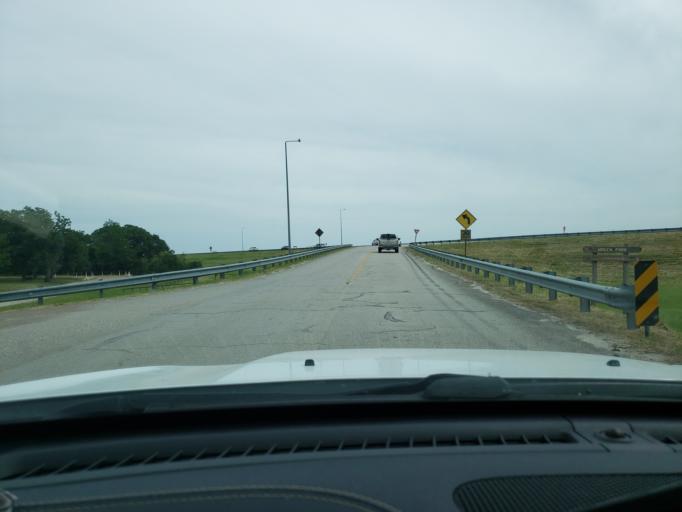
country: US
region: Texas
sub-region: Burleson County
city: Somerville
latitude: 30.3361
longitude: -96.5396
